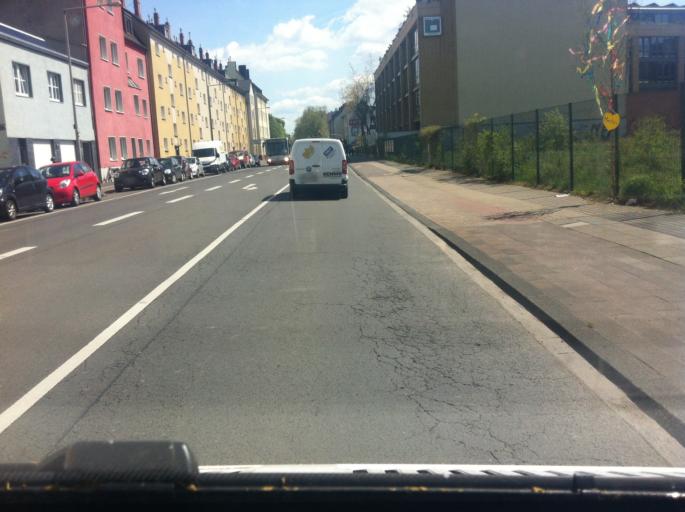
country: DE
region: North Rhine-Westphalia
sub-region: Regierungsbezirk Koln
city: Bilderstoeckchen
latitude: 50.9462
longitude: 6.8954
